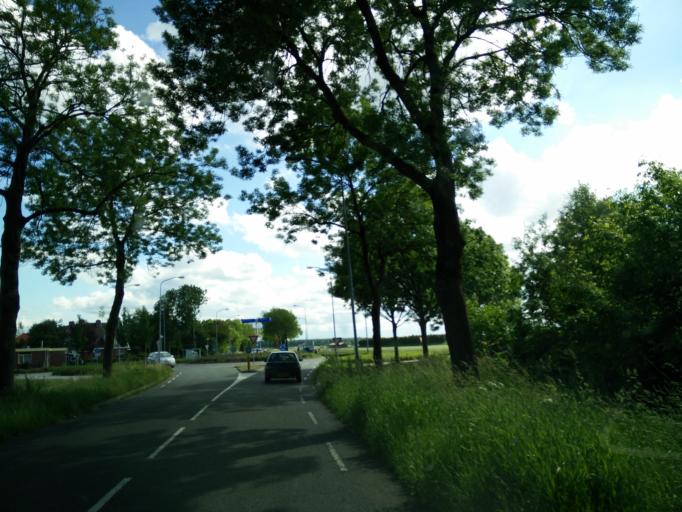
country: NL
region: Groningen
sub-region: Gemeente Bedum
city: Bedum
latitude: 53.2645
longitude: 6.5904
